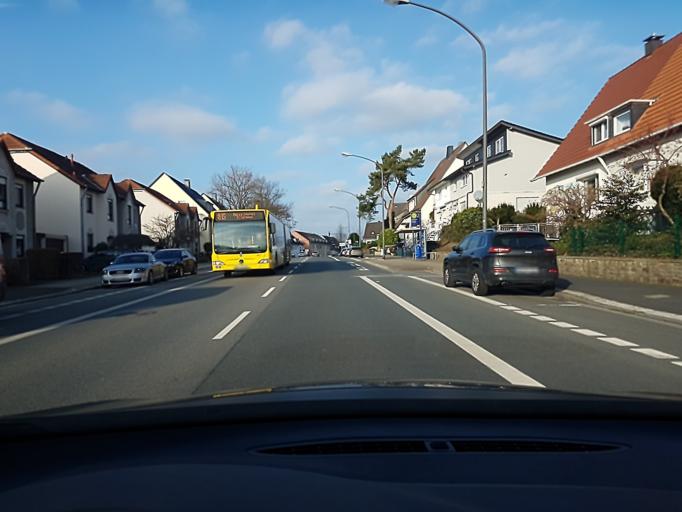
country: DE
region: North Rhine-Westphalia
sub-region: Regierungsbezirk Dusseldorf
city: Essen
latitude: 51.4225
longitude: 7.0871
